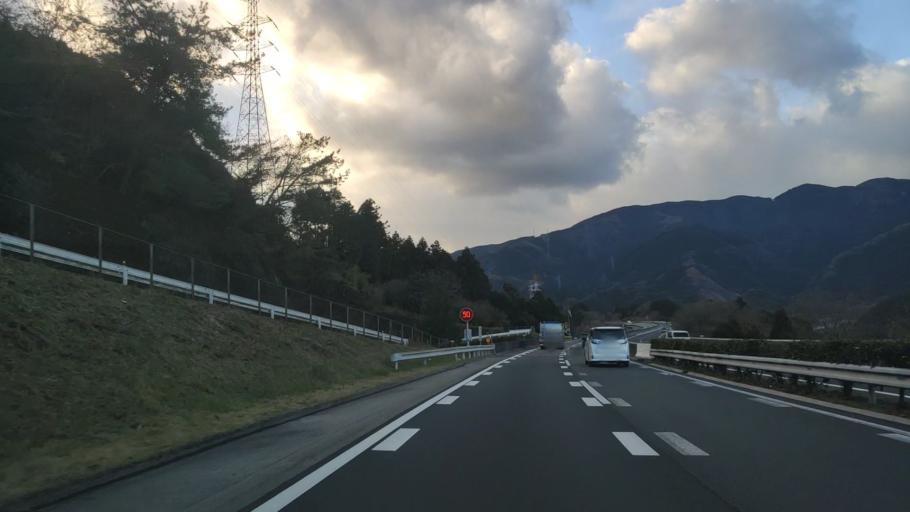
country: JP
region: Ehime
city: Saijo
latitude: 33.8532
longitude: 133.0141
